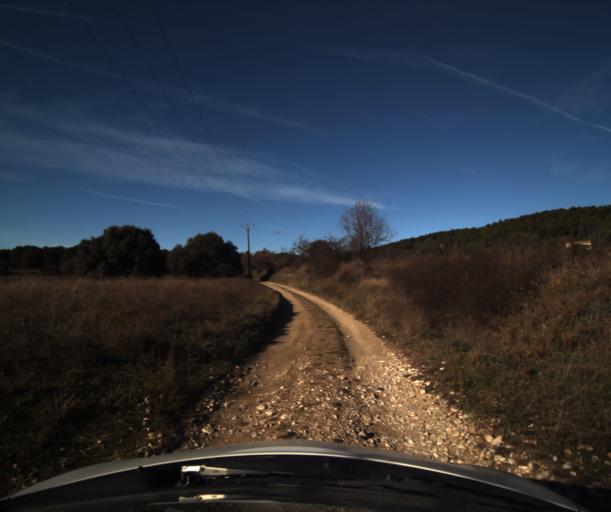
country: FR
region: Provence-Alpes-Cote d'Azur
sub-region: Departement du Vaucluse
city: Pertuis
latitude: 43.7010
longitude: 5.4731
